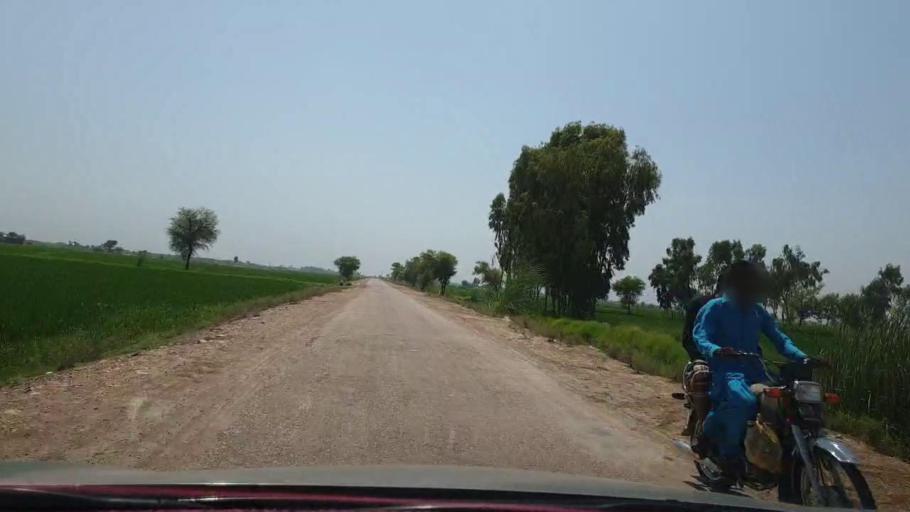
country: PK
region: Sindh
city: Warah
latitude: 27.5597
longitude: 67.7997
